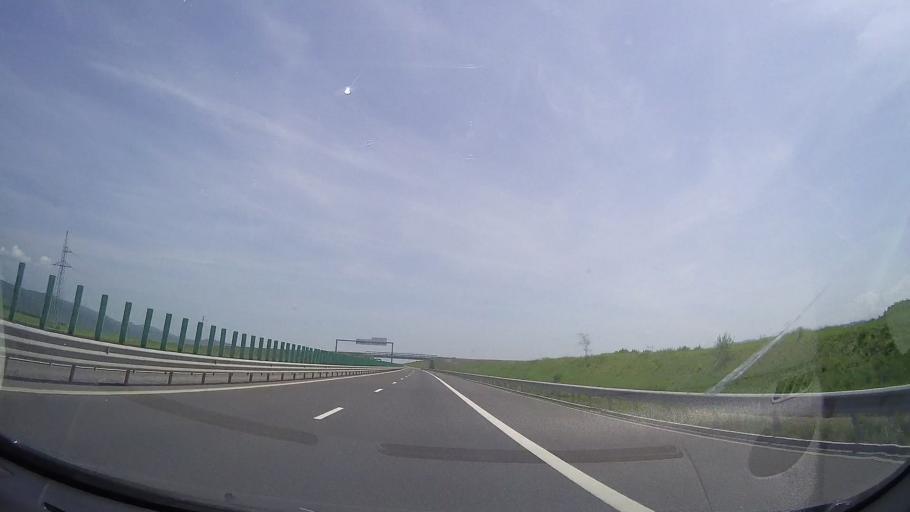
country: RO
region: Hunedoara
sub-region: Comuna Romos
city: Romos
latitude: 45.8946
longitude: 23.2838
